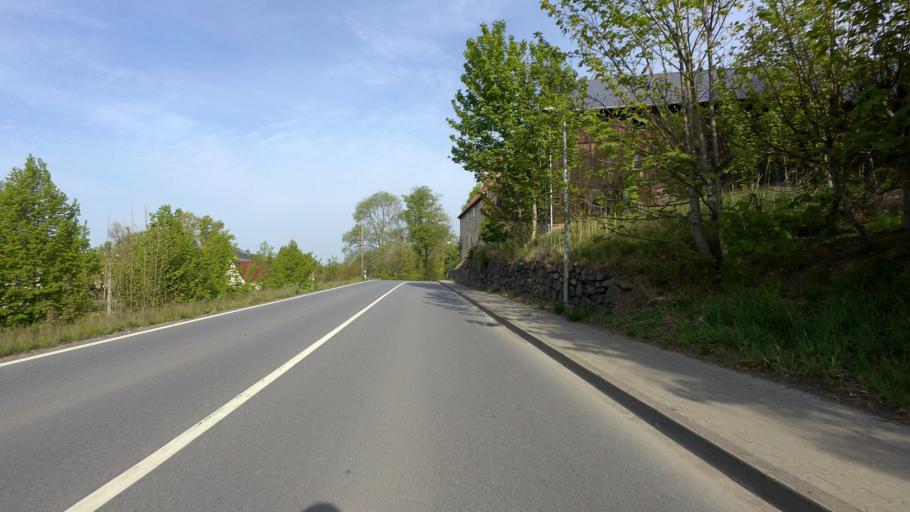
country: DE
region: Saxony
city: Stolpen
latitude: 51.0402
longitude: 14.1274
